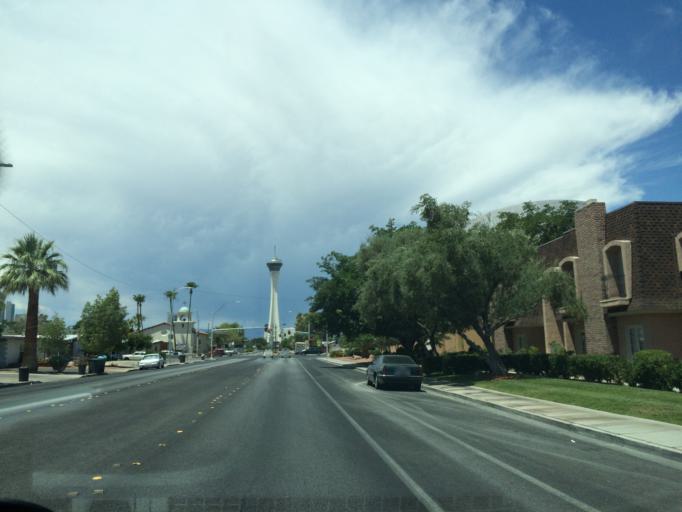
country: US
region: Nevada
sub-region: Clark County
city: Winchester
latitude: 36.1481
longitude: -115.1355
